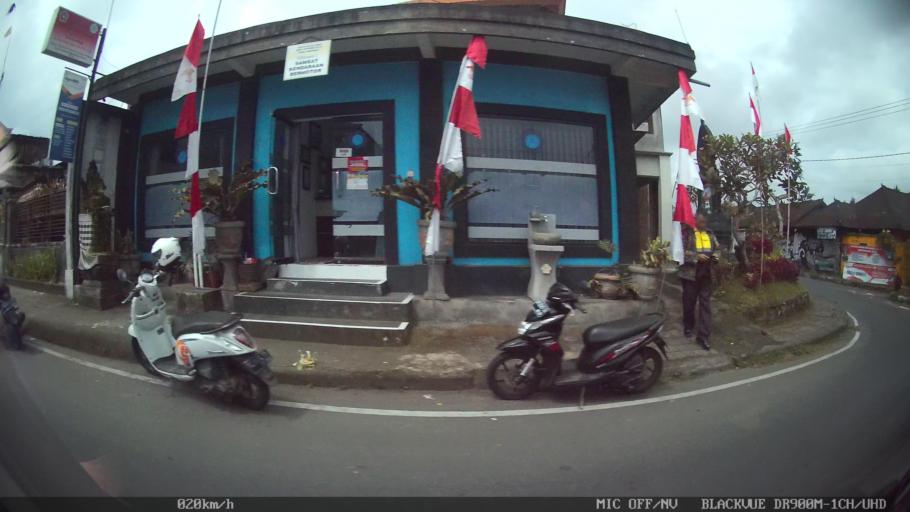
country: ID
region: Bali
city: Banjar Kubu
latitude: -8.4098
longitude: 115.4212
